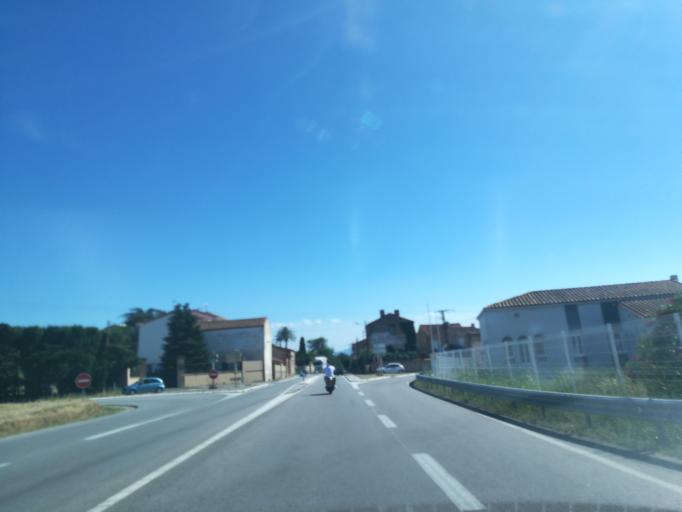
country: FR
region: Languedoc-Roussillon
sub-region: Departement des Pyrenees-Orientales
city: Villemolaque
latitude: 42.6088
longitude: 2.8609
